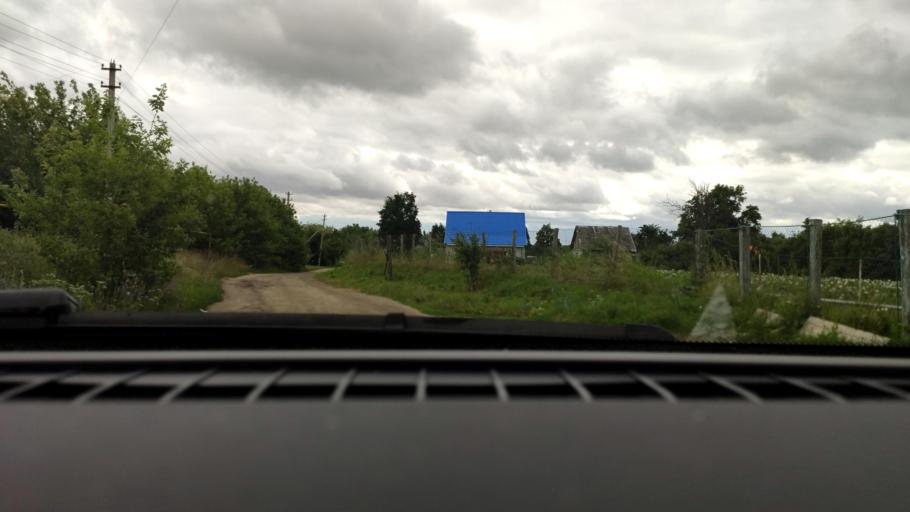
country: RU
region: Voronezj
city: Zemlyansk
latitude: 51.9104
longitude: 38.7249
